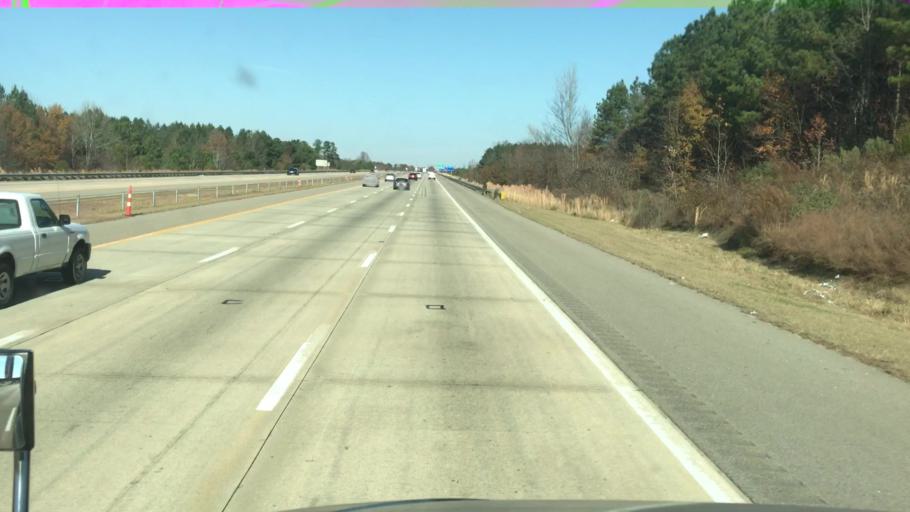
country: US
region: North Carolina
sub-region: Wake County
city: Knightdale
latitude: 35.7914
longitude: -78.4325
